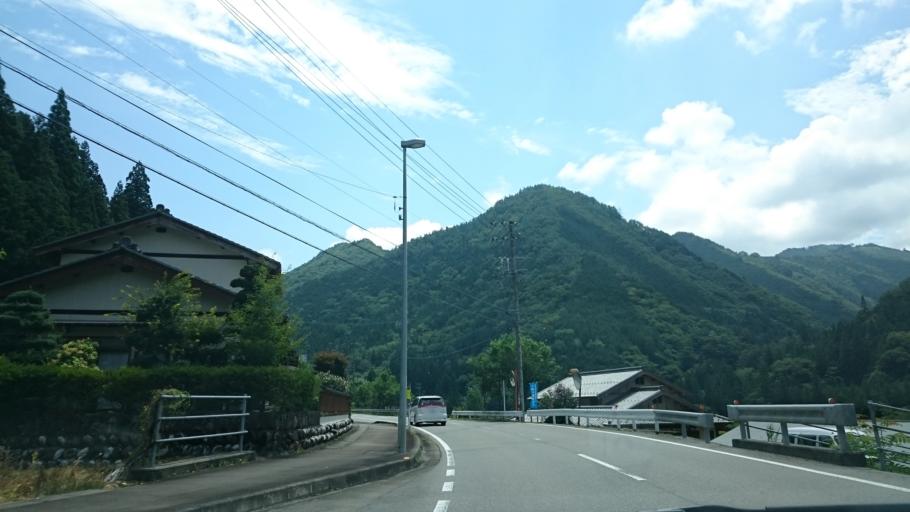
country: JP
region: Gifu
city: Takayama
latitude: 35.9327
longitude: 137.2877
